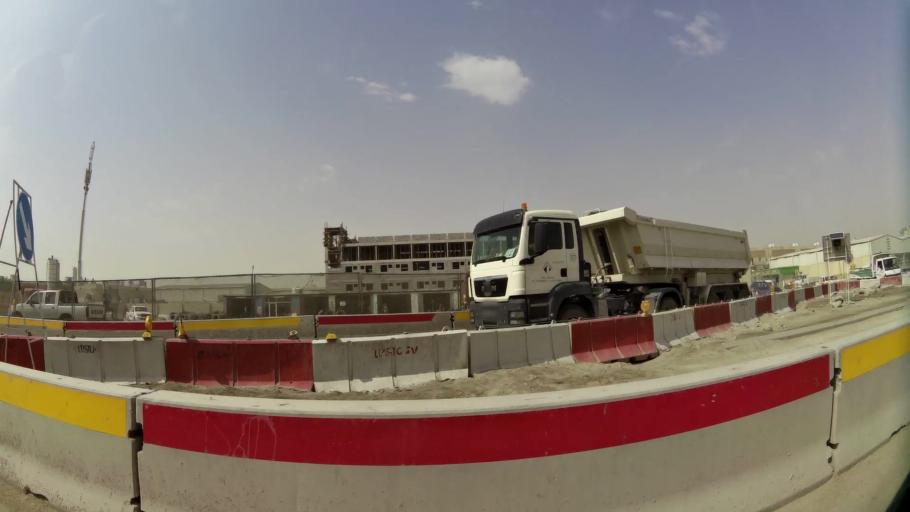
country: QA
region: Al Wakrah
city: Al Wukayr
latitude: 25.1691
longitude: 51.4507
